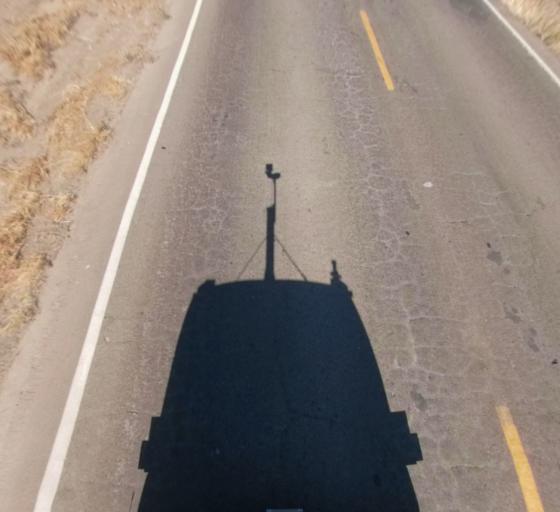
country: US
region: California
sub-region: Fresno County
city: Biola
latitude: 36.8513
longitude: -120.0075
